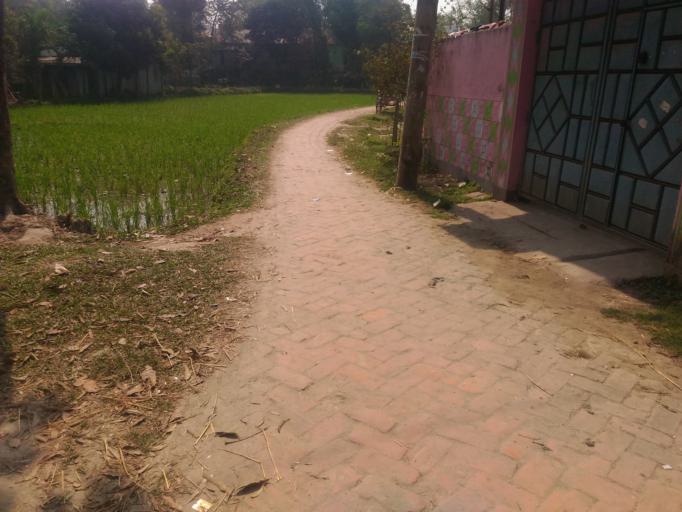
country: BD
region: Dhaka
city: Tungi
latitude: 24.0119
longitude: 90.3798
